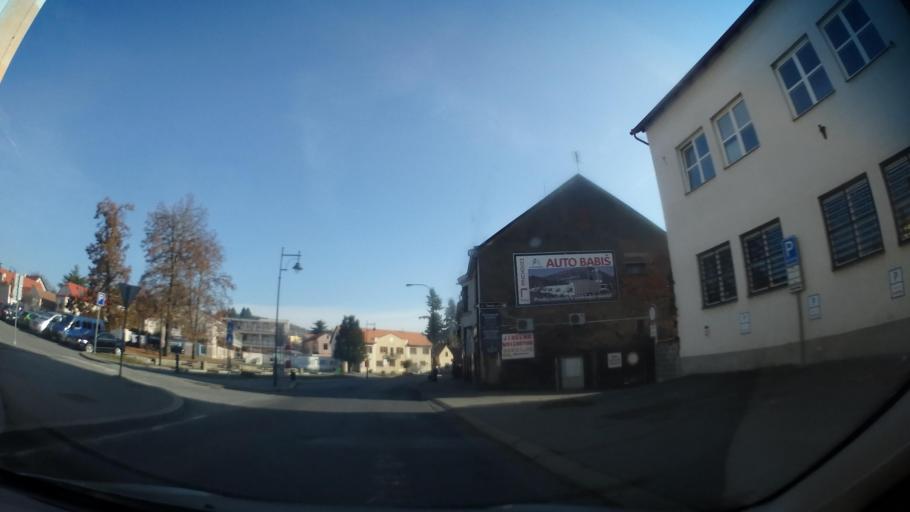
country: CZ
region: Central Bohemia
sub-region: Okres Praha-Vychod
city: Mnichovice
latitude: 49.9361
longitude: 14.7090
